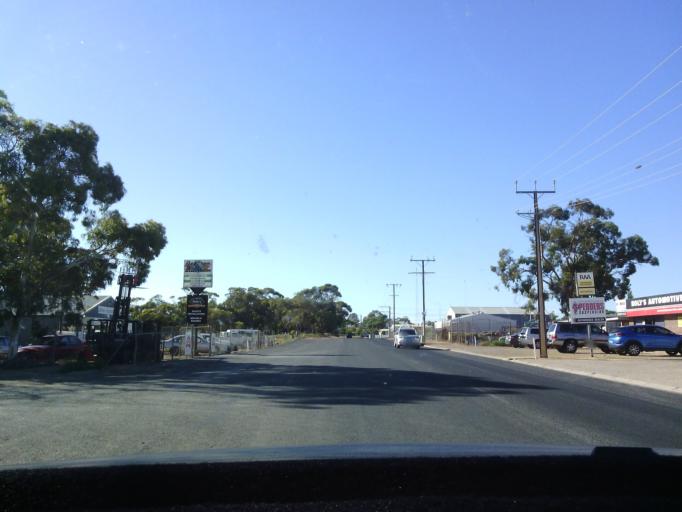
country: AU
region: South Australia
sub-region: Berri and Barmera
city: Berri
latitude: -34.2688
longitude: 140.6036
